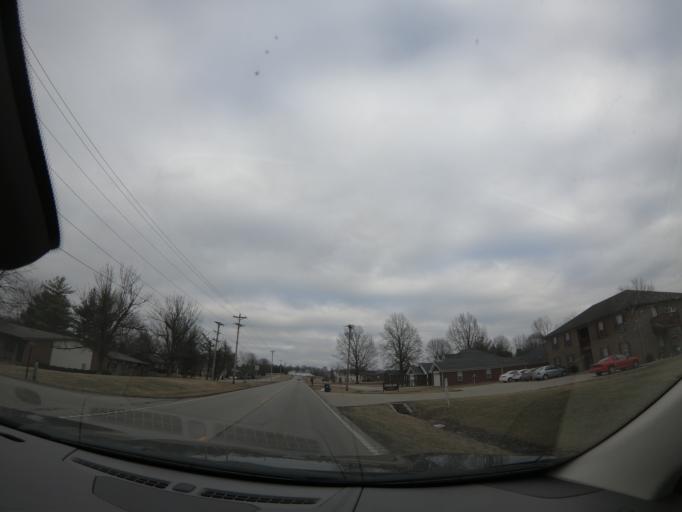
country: US
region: Kentucky
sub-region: Nelson County
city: Bardstown
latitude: 37.8294
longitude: -85.4166
